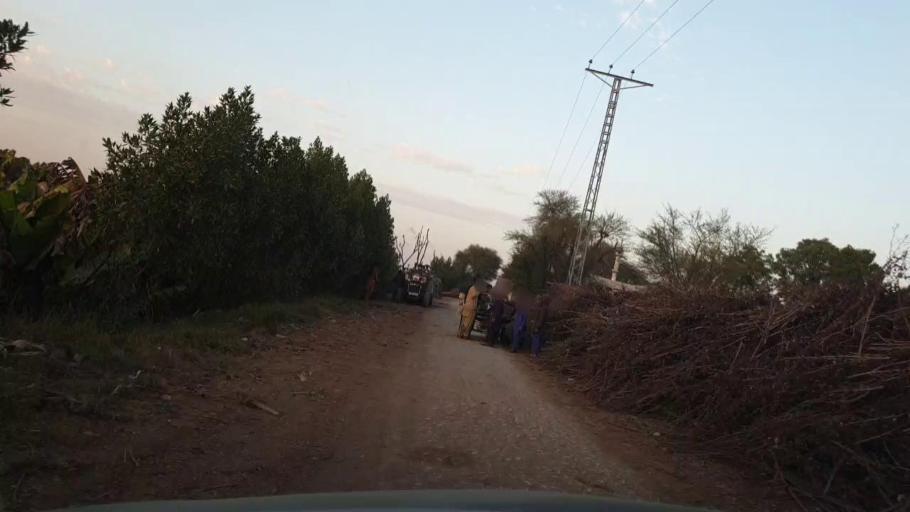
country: PK
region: Sindh
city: Matiari
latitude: 25.6076
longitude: 68.4817
